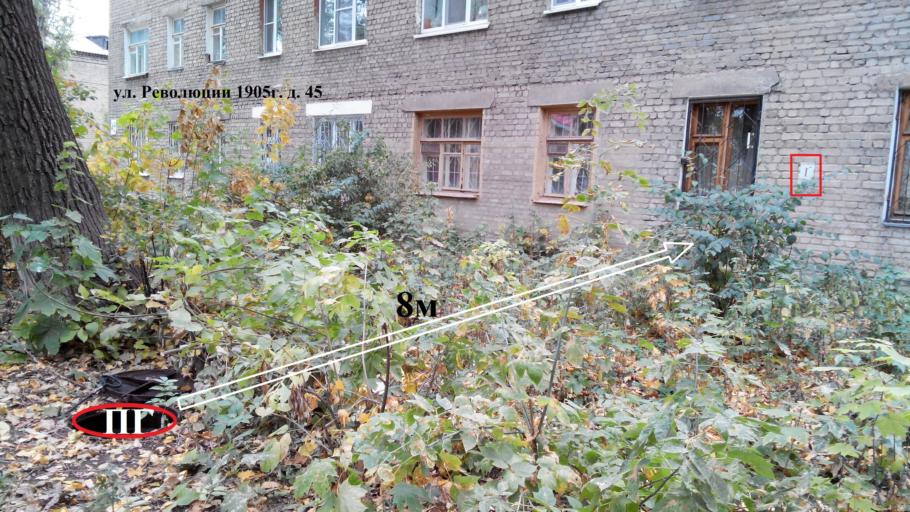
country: RU
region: Voronezj
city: Voronezh
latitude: 51.6591
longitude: 39.1802
